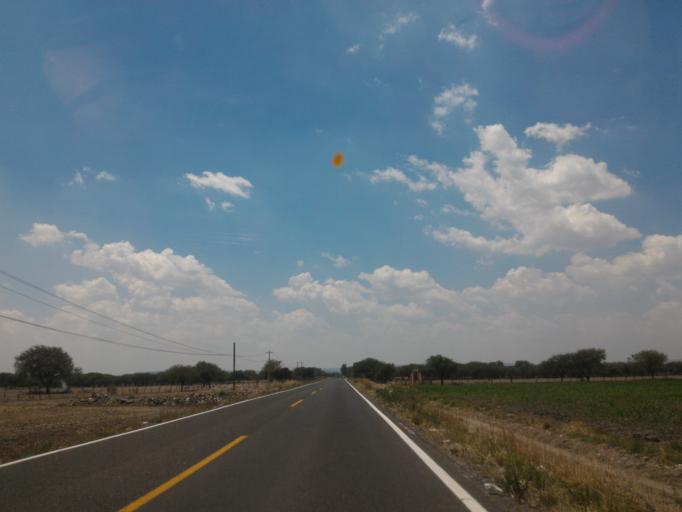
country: MX
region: Guanajuato
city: Ciudad Manuel Doblado
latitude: 20.7667
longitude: -101.9710
